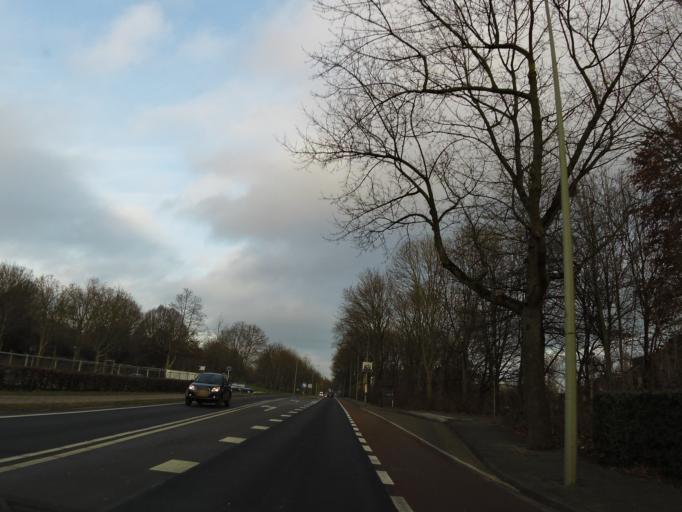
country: NL
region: Limburg
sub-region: Gemeente Heerlen
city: Hoensbroek
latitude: 50.9256
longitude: 5.9137
